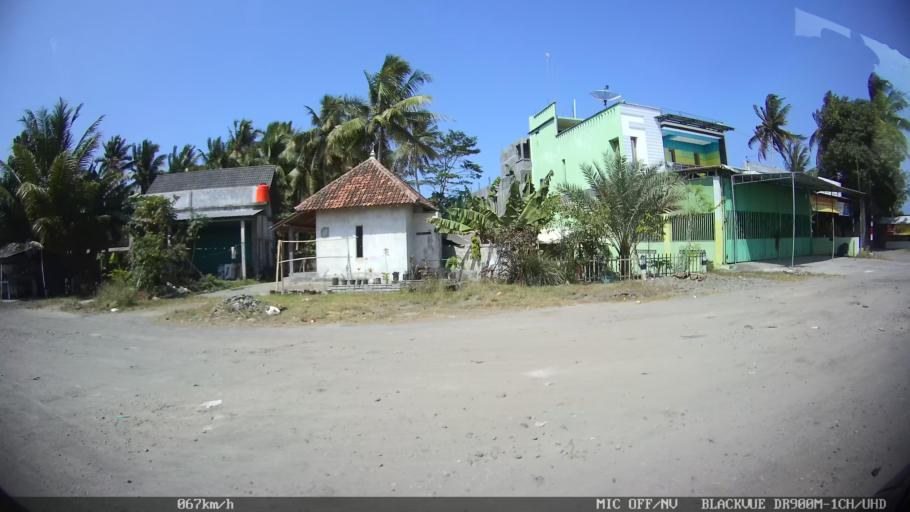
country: ID
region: Daerah Istimewa Yogyakarta
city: Srandakan
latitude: -7.9532
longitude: 110.1938
